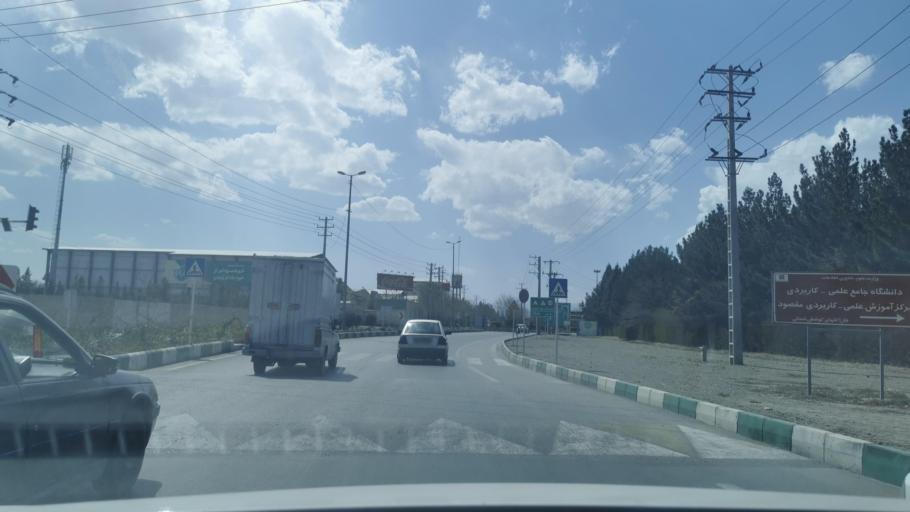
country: IR
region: Razavi Khorasan
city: Torqabeh
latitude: 36.4295
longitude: 59.4185
